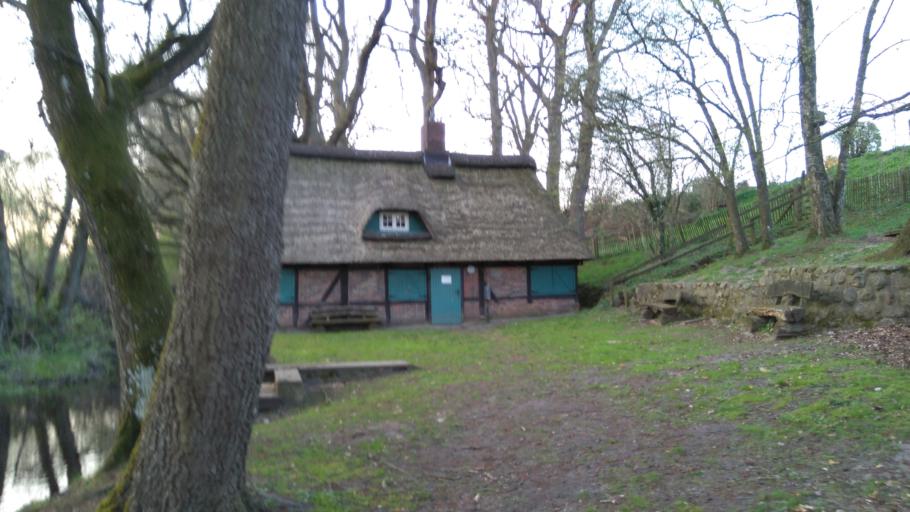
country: DE
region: Lower Saxony
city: Bargstedt
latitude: 53.4586
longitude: 9.4668
